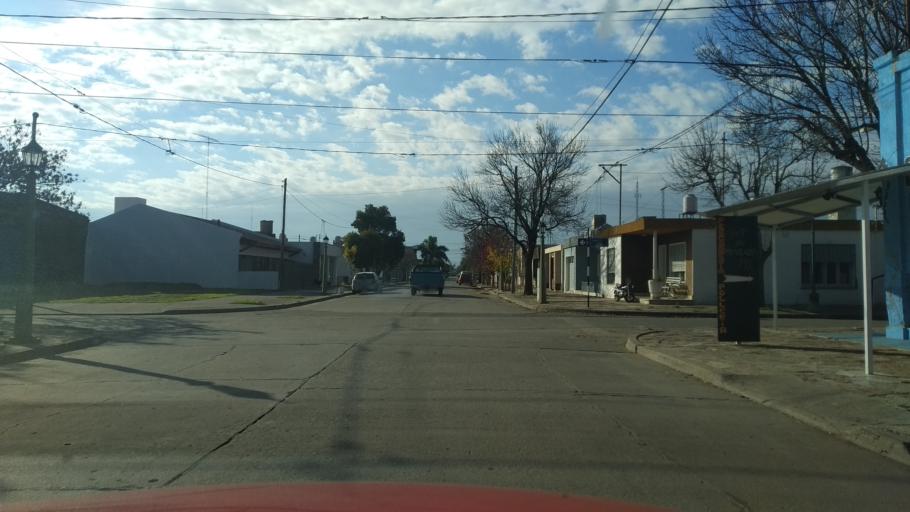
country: AR
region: Cordoba
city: Leones
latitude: -32.6573
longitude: -62.3003
